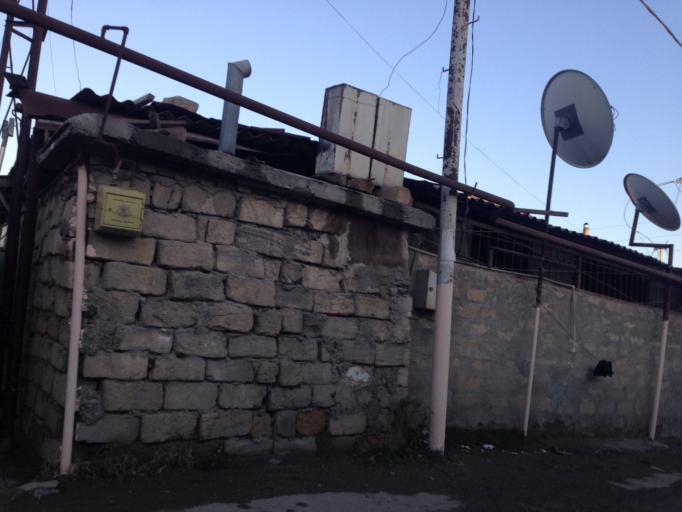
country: AZ
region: Baki
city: Baku
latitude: 40.4162
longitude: 49.8653
